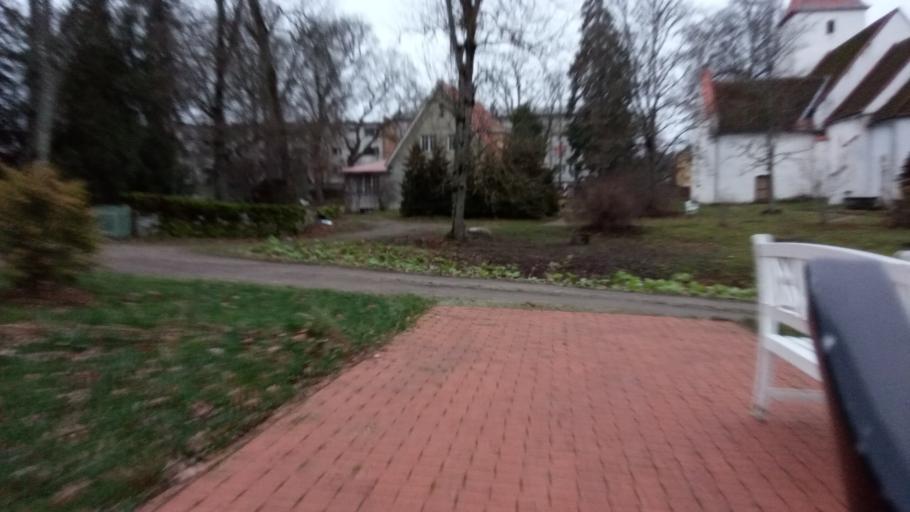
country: EE
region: Harju
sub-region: Kuusalu vald
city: Kuusalu
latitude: 59.4451
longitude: 25.4380
